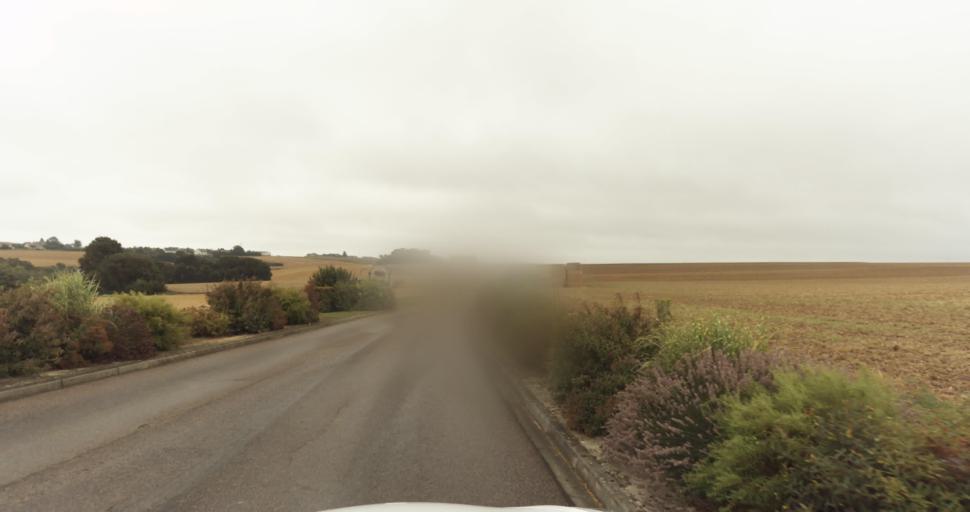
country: FR
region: Haute-Normandie
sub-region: Departement de l'Eure
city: Gravigny
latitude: 49.0800
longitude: 1.2128
